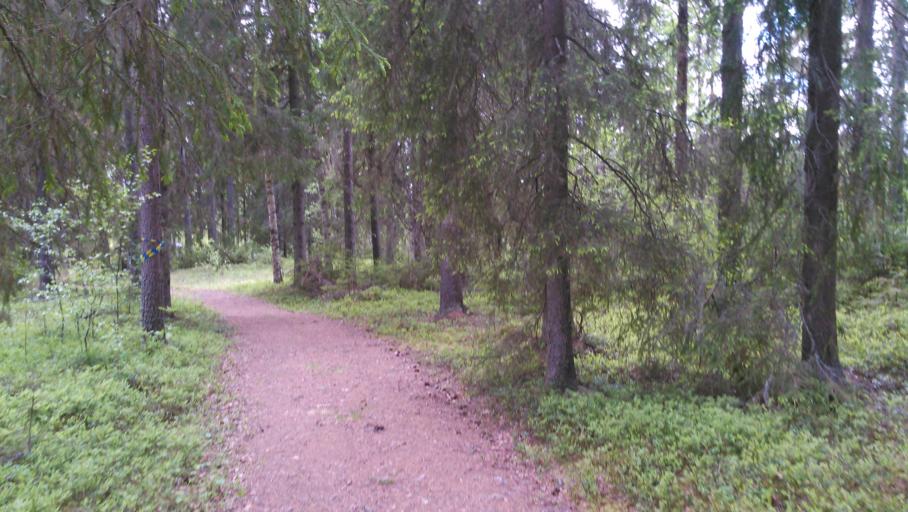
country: SE
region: Vaesterbotten
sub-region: Vannas Kommun
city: Vannasby
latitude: 64.0168
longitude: 19.9017
